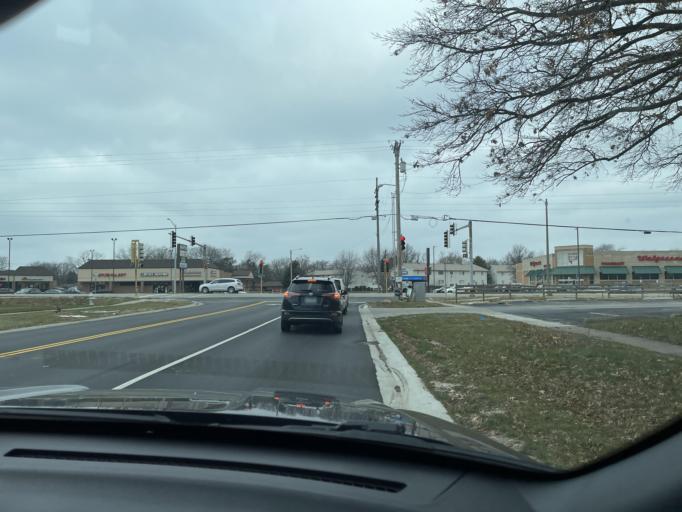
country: US
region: Illinois
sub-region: Sangamon County
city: Leland Grove
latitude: 39.7947
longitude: -89.6944
